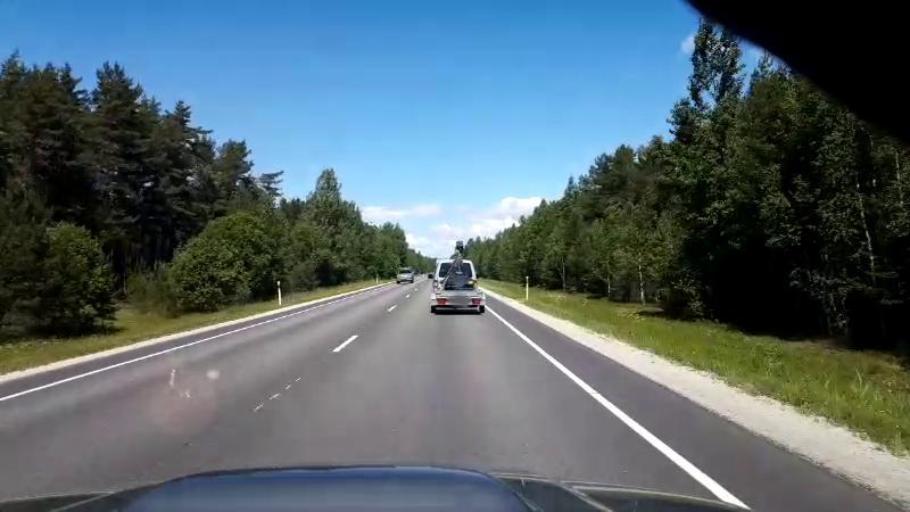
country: LV
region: Salacgrivas
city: Ainazi
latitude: 58.0984
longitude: 24.5081
